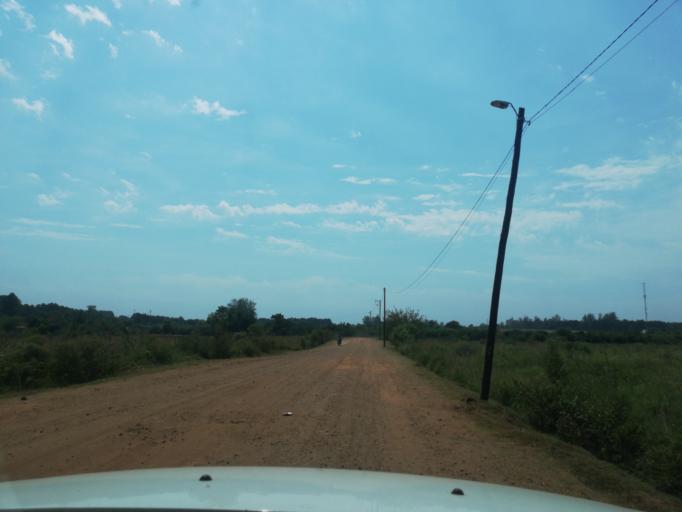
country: AR
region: Misiones
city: Garupa
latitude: -27.4501
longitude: -55.8940
